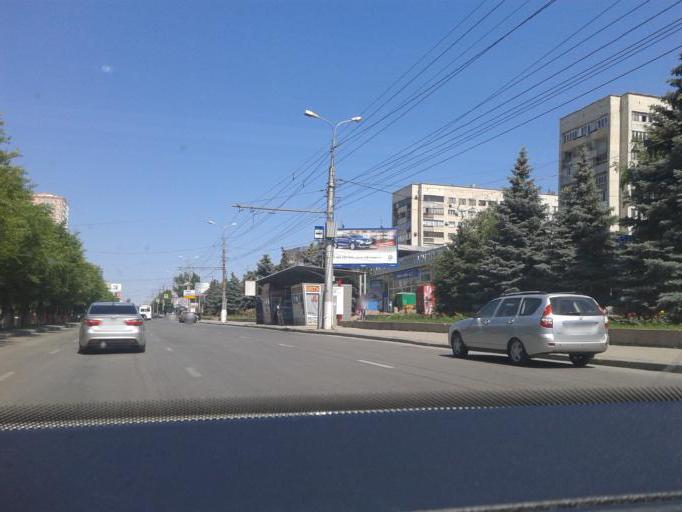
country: RU
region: Volgograd
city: Volgograd
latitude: 48.7181
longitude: 44.5082
